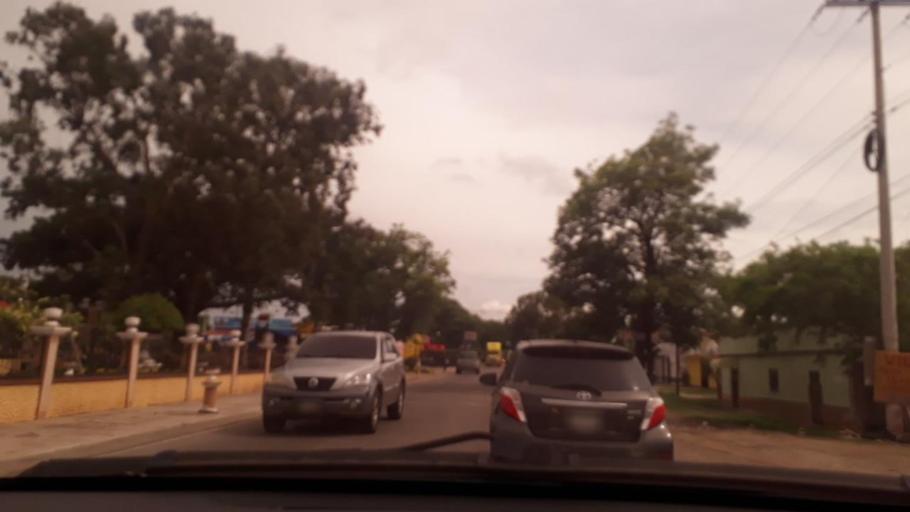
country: GT
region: Jutiapa
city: El Progreso
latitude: 14.3282
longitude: -89.8596
